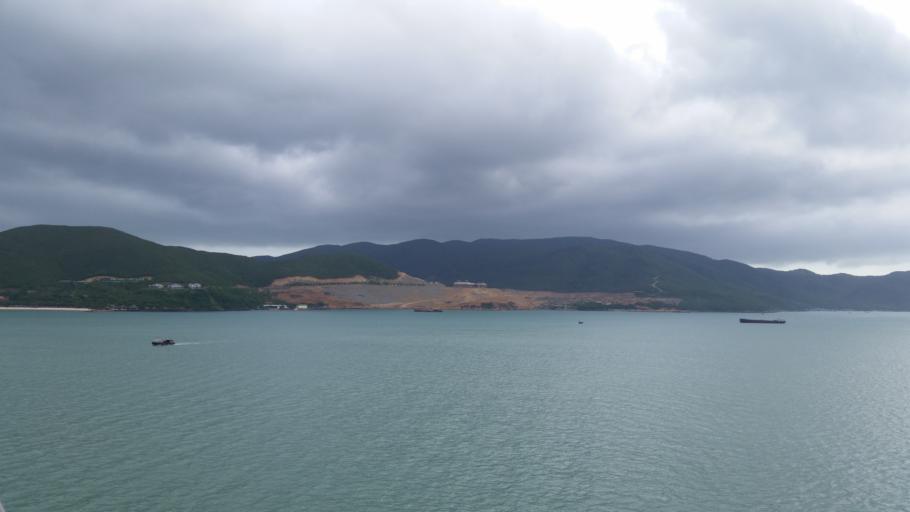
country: VN
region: Khanh Hoa
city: Nha Trang
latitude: 12.2012
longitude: 109.2335
